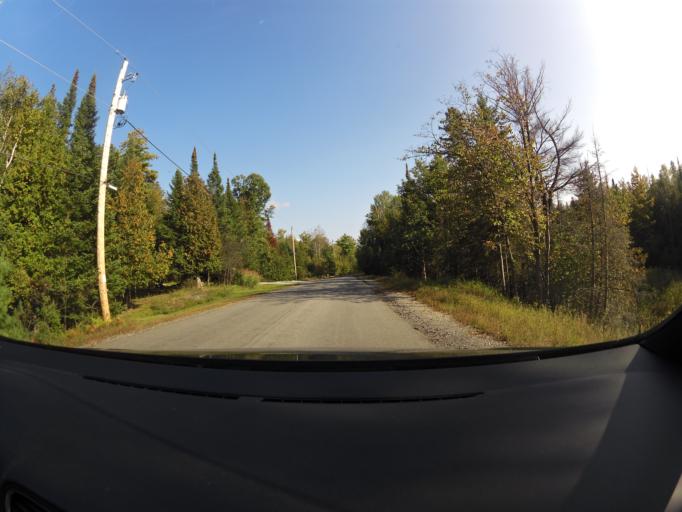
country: CA
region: Ontario
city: Arnprior
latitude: 45.4615
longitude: -76.2791
